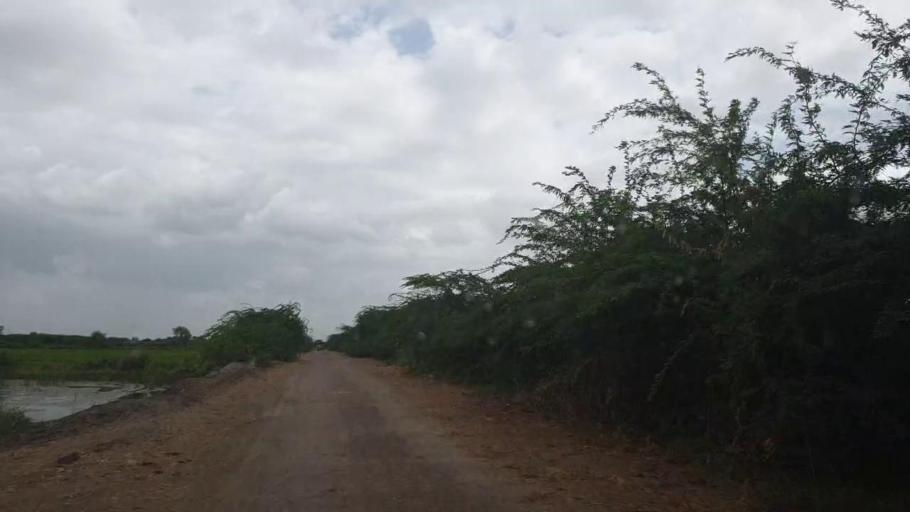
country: PK
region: Sindh
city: Badin
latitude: 24.6455
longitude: 68.9458
